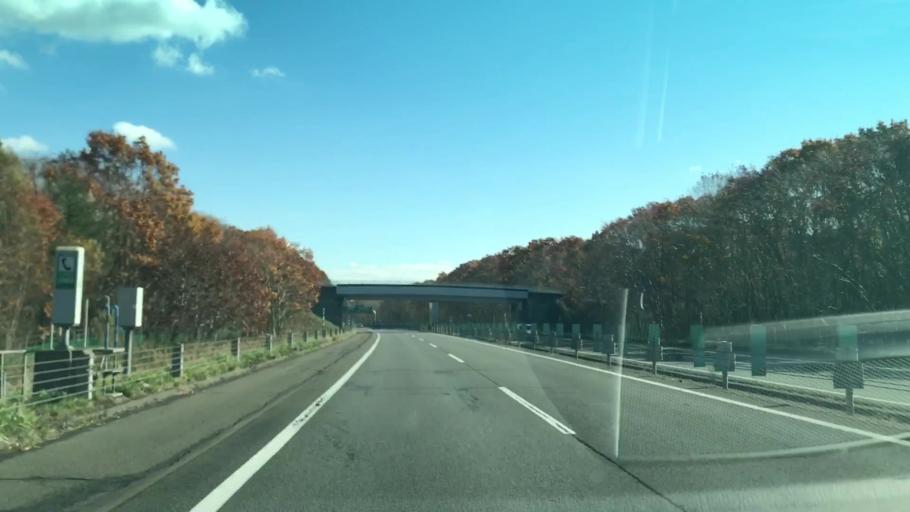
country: JP
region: Hokkaido
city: Chitose
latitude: 42.8518
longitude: 141.5687
